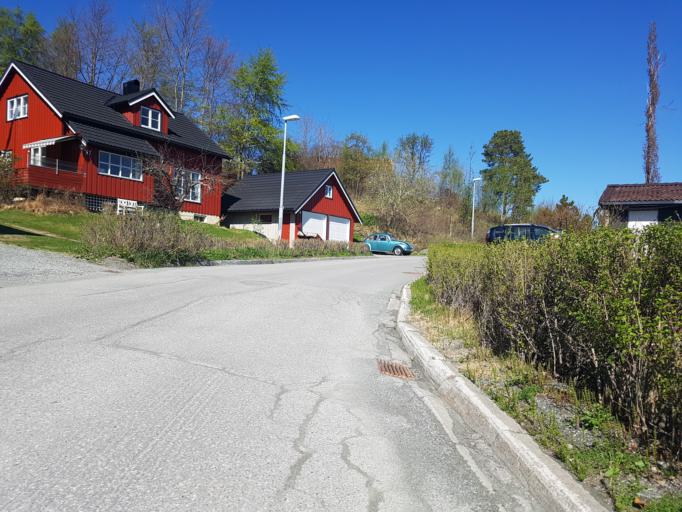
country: NO
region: Sor-Trondelag
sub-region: Trondheim
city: Trondheim
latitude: 63.4247
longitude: 10.3462
